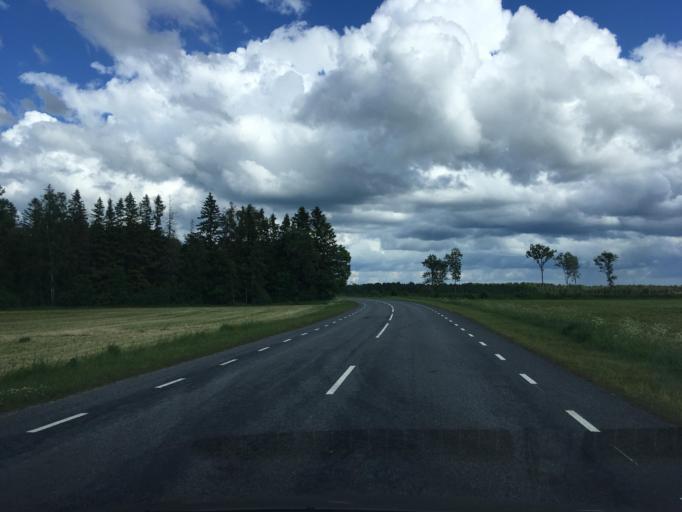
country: EE
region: Paernumaa
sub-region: Halinga vald
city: Parnu-Jaagupi
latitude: 58.6128
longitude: 24.4645
